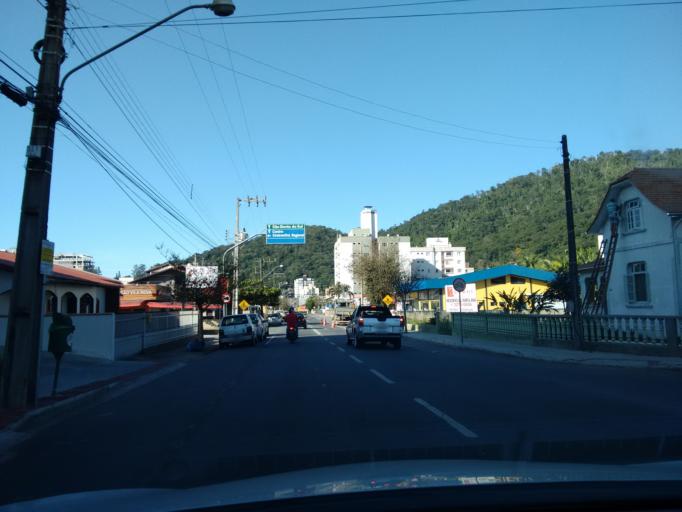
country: BR
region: Santa Catarina
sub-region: Jaragua Do Sul
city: Jaragua do Sul
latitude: -26.5005
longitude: -49.0856
